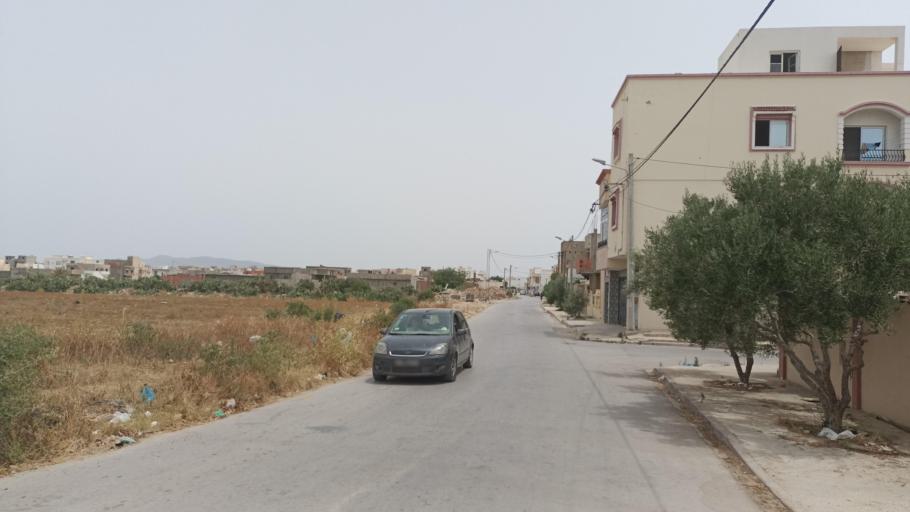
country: TN
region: Nabul
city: Manzil Bu Zalafah
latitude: 36.6985
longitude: 10.4825
